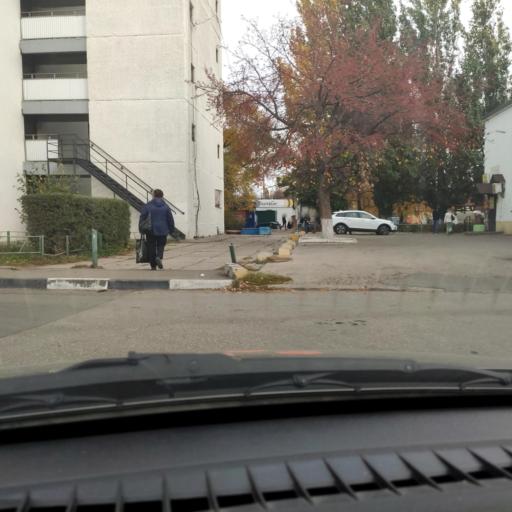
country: RU
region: Samara
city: Tol'yatti
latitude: 53.5105
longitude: 49.2700
